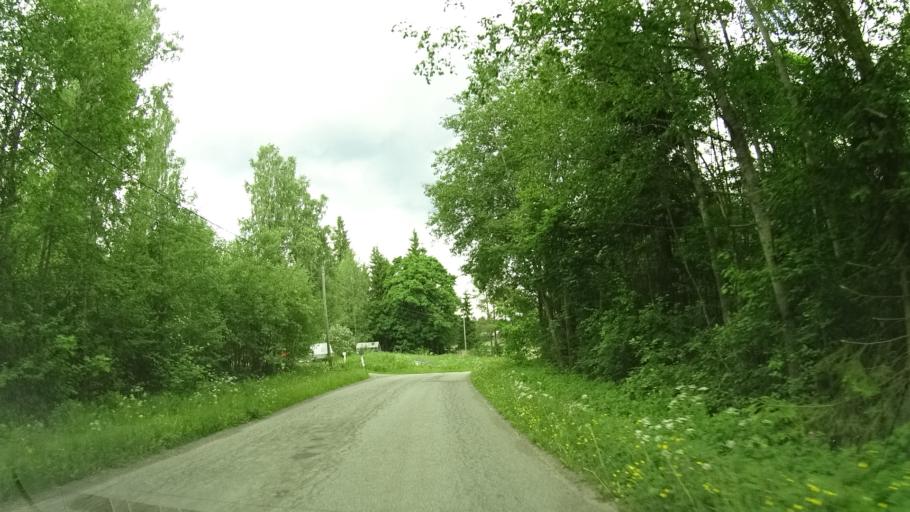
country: FI
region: Uusimaa
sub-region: Helsinki
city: Siuntio
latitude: 60.2117
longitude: 24.2379
